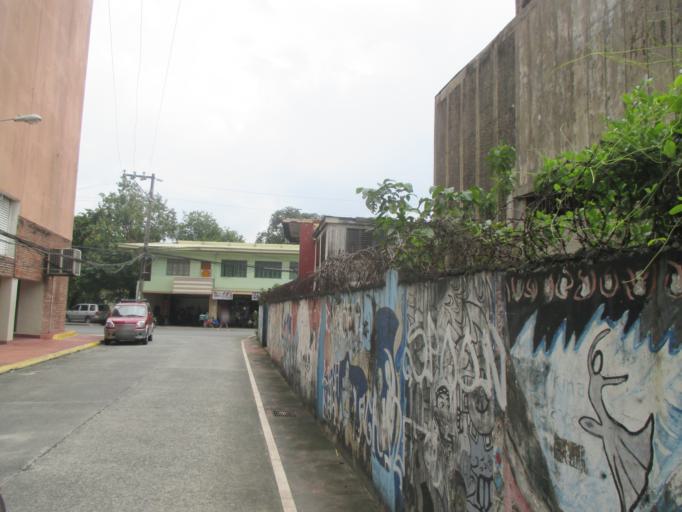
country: PH
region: Metro Manila
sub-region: Marikina
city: Calumpang
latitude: 14.6297
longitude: 121.0977
